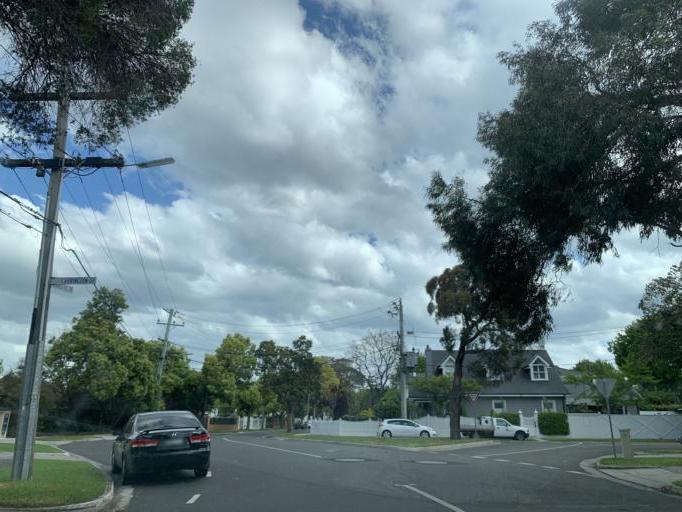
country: AU
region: Victoria
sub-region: Bayside
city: North Brighton
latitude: -37.9174
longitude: 145.0128
